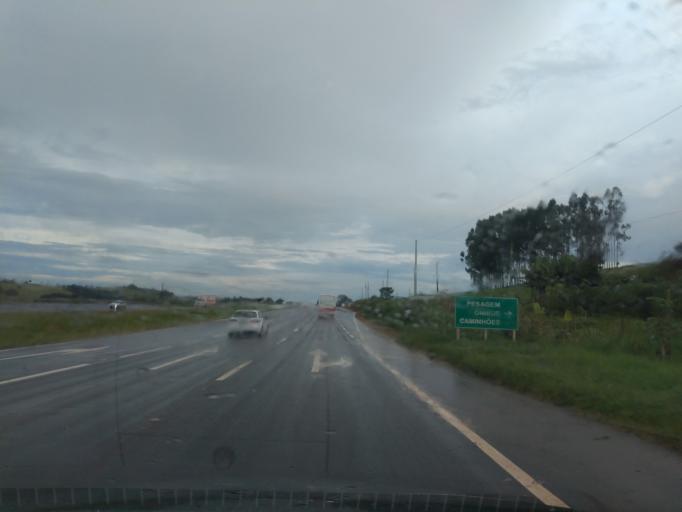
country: BR
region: Minas Gerais
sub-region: Tres Coracoes
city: Tres Coracoes
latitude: -21.6500
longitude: -45.3608
